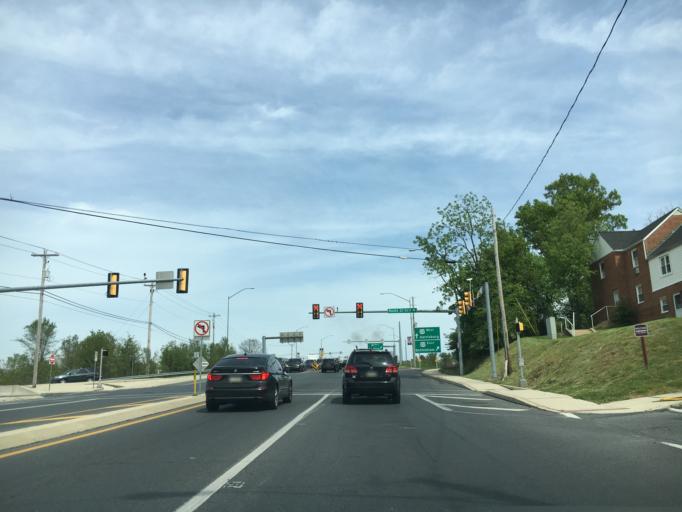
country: US
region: Pennsylvania
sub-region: Lehigh County
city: Fullerton
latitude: 40.6252
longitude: -75.4824
